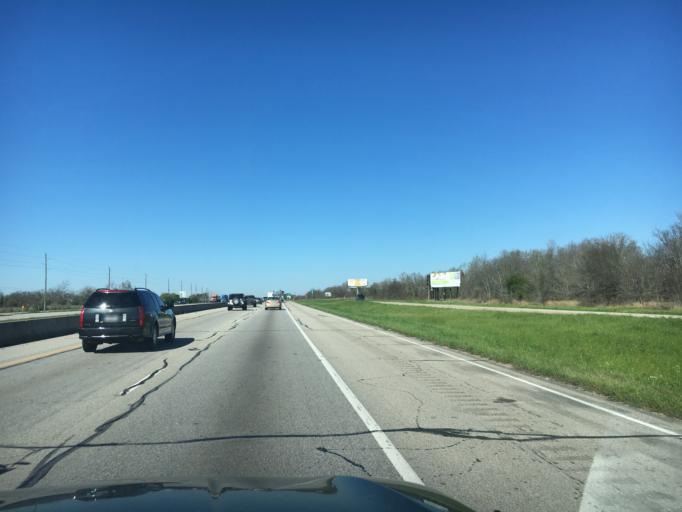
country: US
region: Texas
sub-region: Austin County
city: Sealy
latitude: 29.7720
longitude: -96.0620
